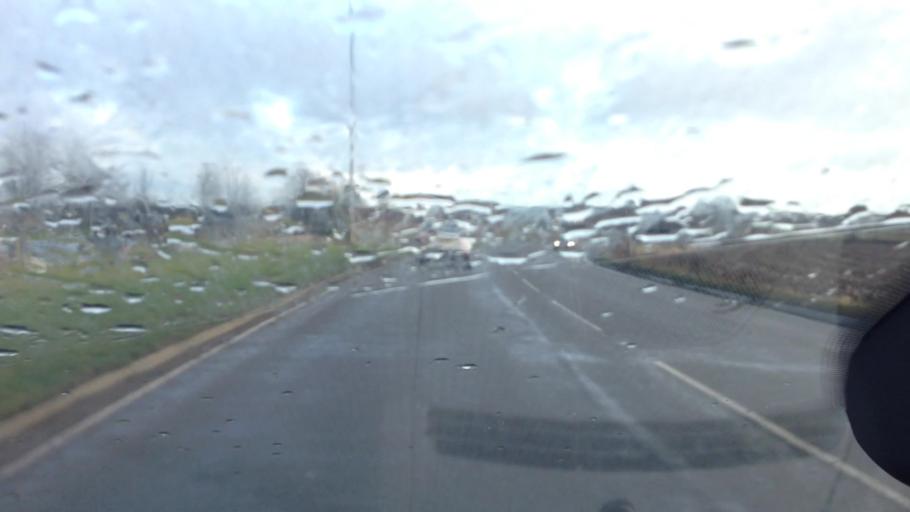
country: GB
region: England
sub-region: City and Borough of Leeds
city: Garforth
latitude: 53.7809
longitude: -1.3661
